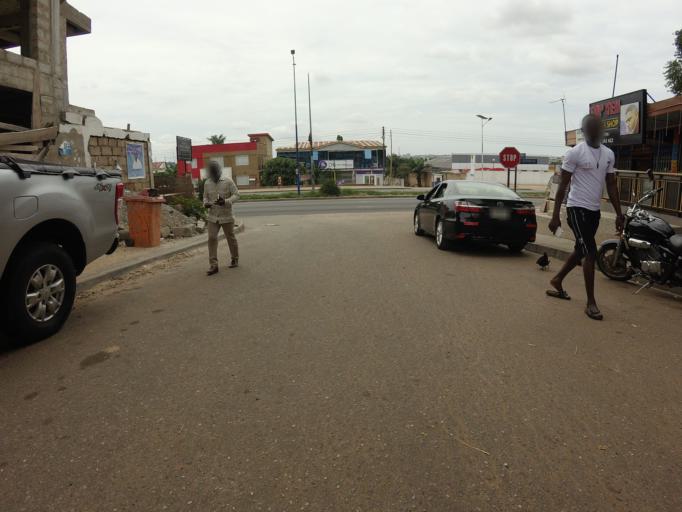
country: GH
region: Greater Accra
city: Accra
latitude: 5.5975
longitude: -0.2233
